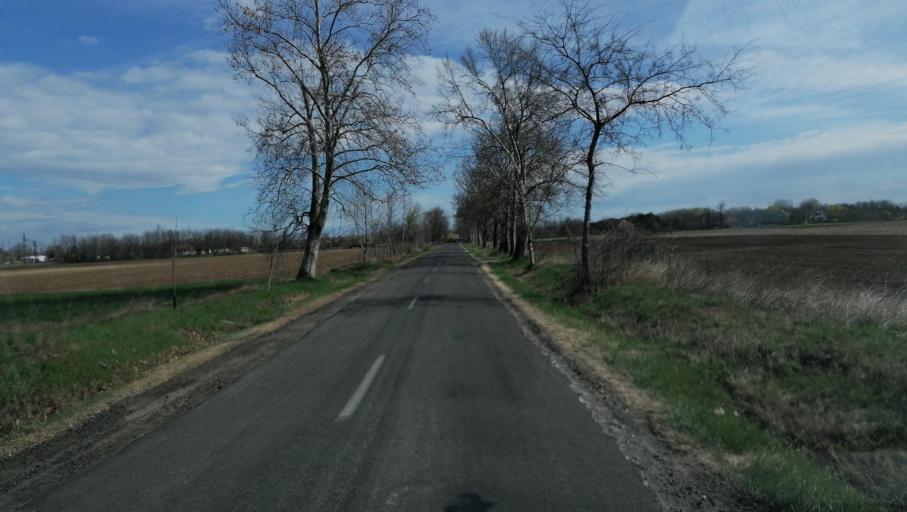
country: HU
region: Pest
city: Ujhartyan
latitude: 47.1903
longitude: 19.3702
